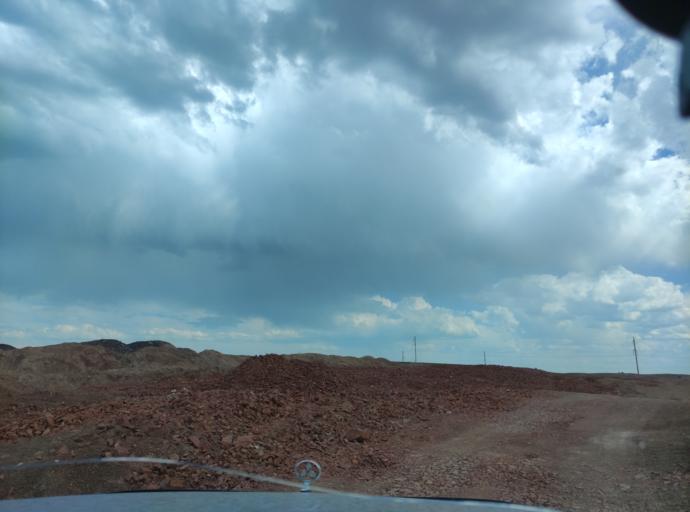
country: KZ
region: Qaraghandy
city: Saryshaghan
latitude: 46.1257
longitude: 73.5966
